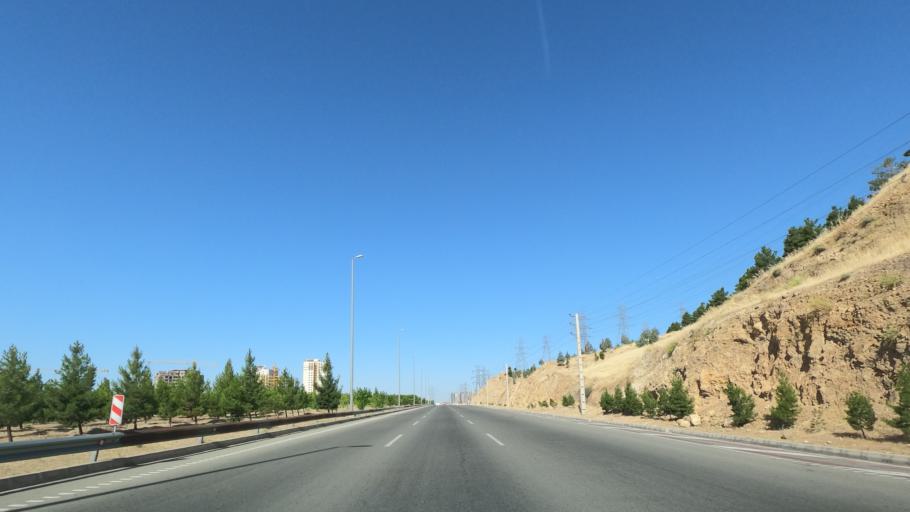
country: IR
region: Tehran
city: Shahr-e Qods
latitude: 35.7562
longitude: 51.1373
